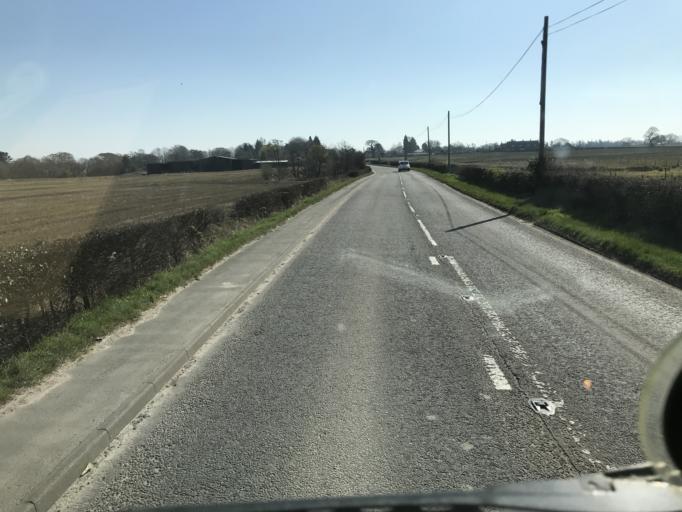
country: GB
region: England
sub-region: Cheshire East
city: Mobberley
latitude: 53.2749
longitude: -2.2945
